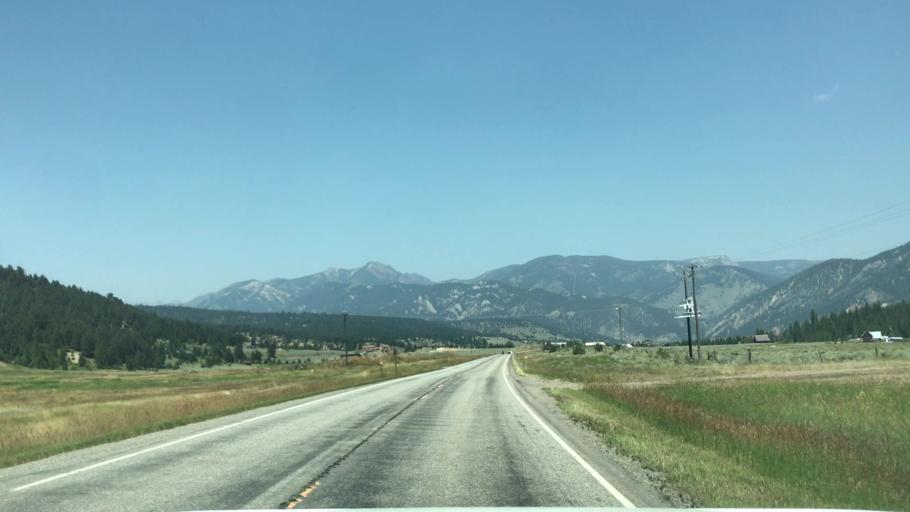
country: US
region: Montana
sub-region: Gallatin County
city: Big Sky
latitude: 45.2126
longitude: -111.2477
